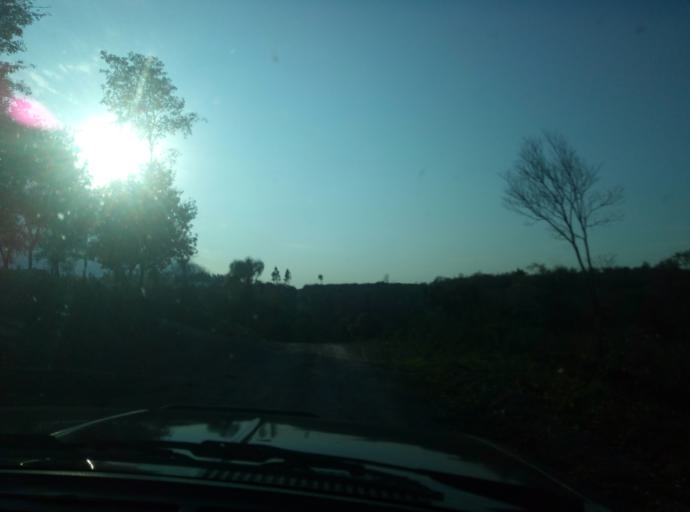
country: PY
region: Caaguazu
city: Doctor Cecilio Baez
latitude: -25.1987
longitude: -56.1265
